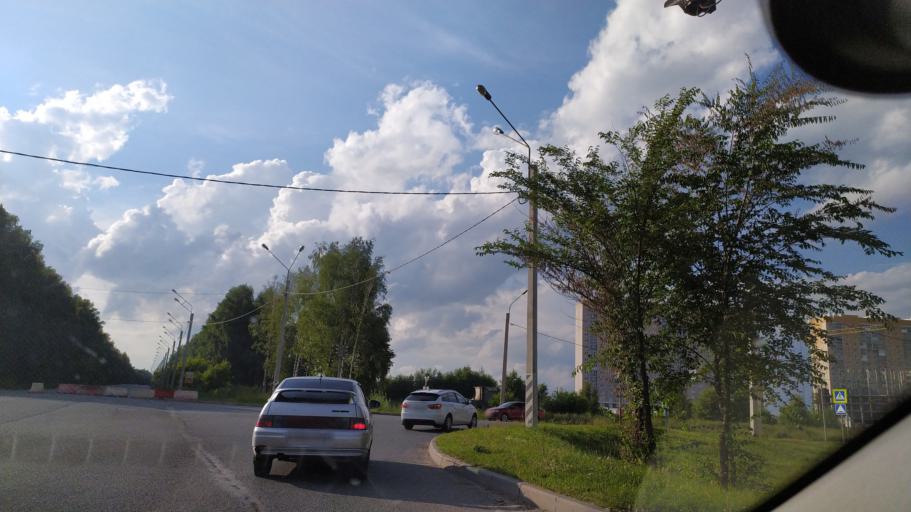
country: RU
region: Chuvashia
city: Novocheboksarsk
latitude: 56.1134
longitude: 47.4404
